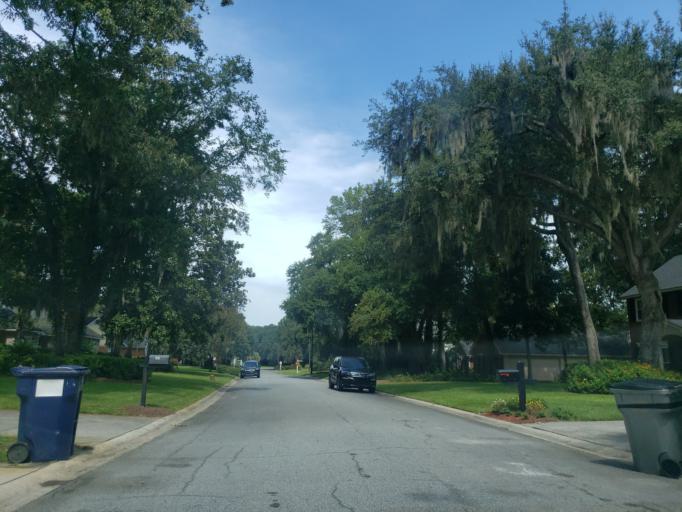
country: US
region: Georgia
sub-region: Chatham County
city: Wilmington Island
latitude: 32.0027
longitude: -80.9744
